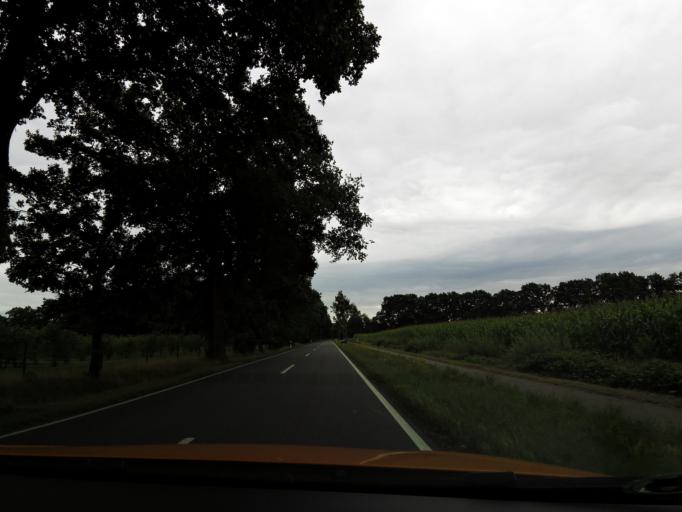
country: DE
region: Lower Saxony
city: Wiefelstede
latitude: 53.1941
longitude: 8.1386
